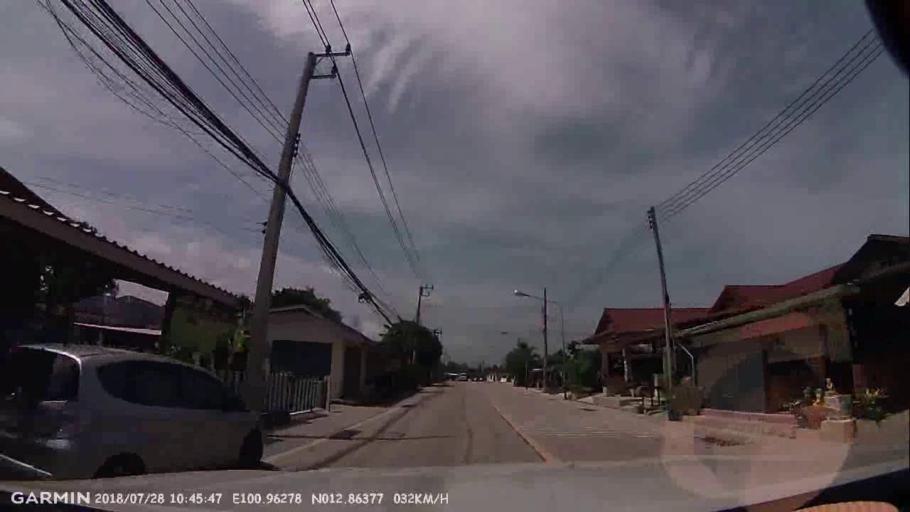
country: TH
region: Chon Buri
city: Phatthaya
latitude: 12.8637
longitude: 100.9628
